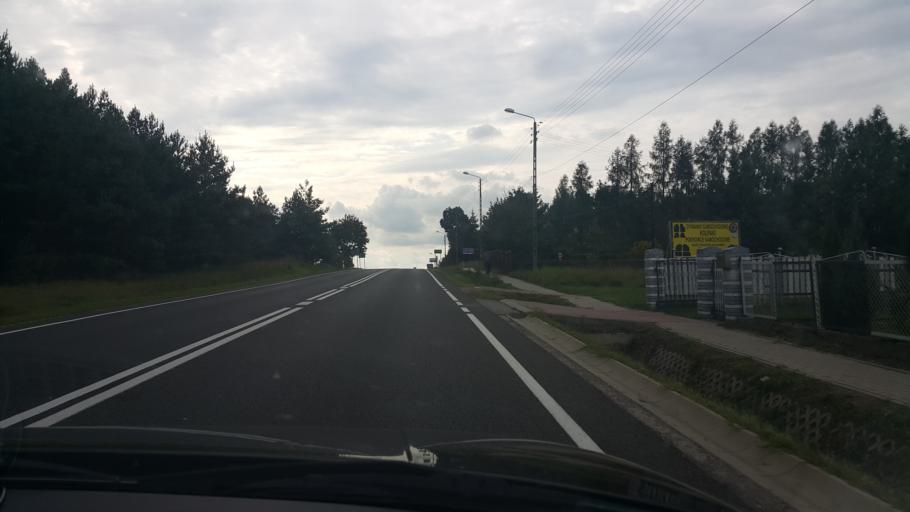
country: PL
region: Swietokrzyskie
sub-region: Powiat skarzyski
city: Blizyn
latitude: 51.0989
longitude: 20.7975
